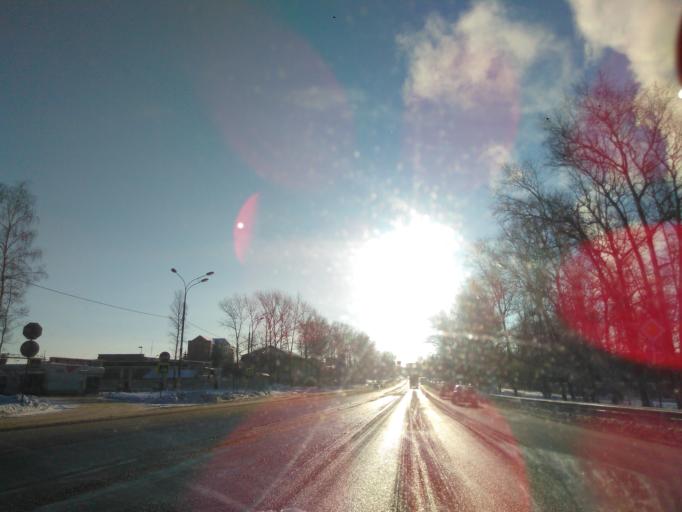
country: RU
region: Moskovskaya
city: Klin
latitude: 56.3467
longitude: 36.7077
